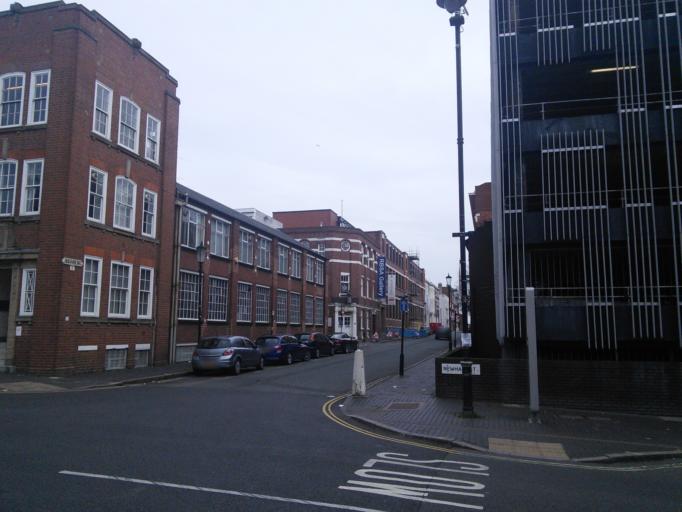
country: GB
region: England
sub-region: City and Borough of Birmingham
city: Birmingham
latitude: 52.4845
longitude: -1.9080
